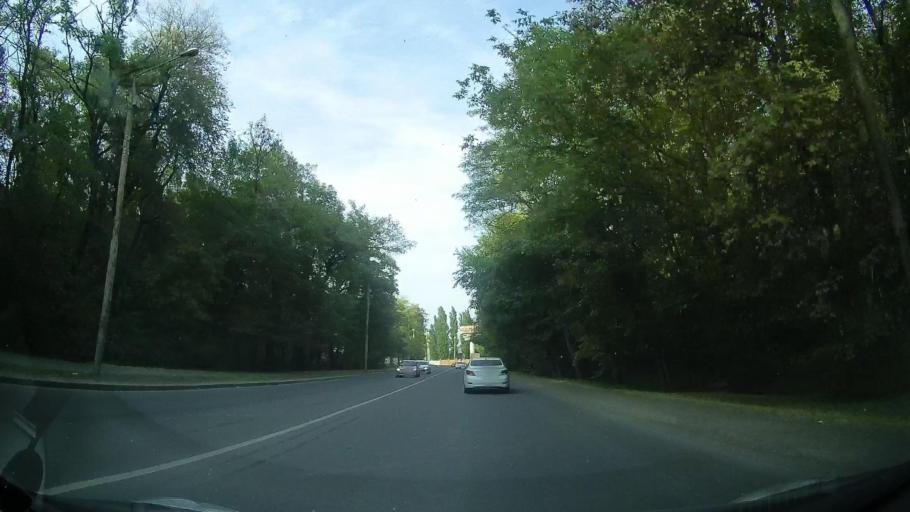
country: RU
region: Rostov
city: Imeni Chkalova
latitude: 47.2771
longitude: 39.7963
